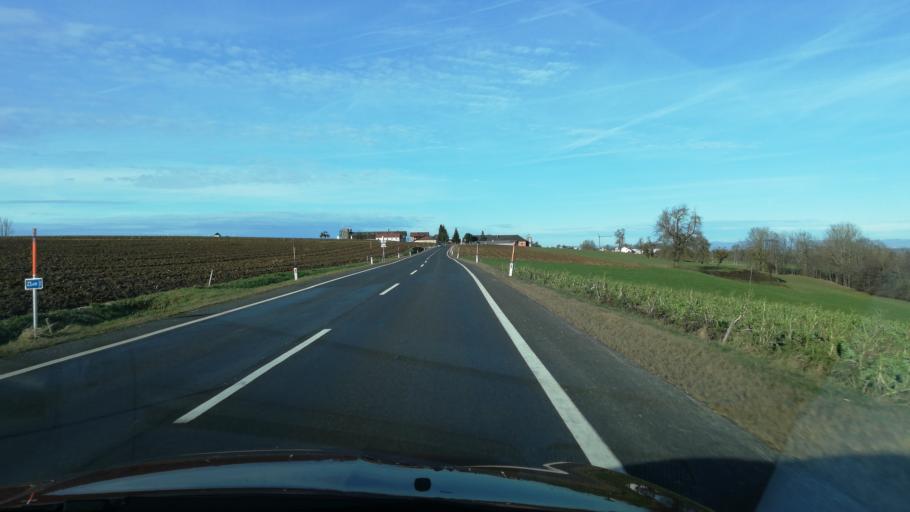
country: AT
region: Upper Austria
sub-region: Politischer Bezirk Kirchdorf an der Krems
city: Kremsmunster
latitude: 47.9699
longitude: 14.0788
